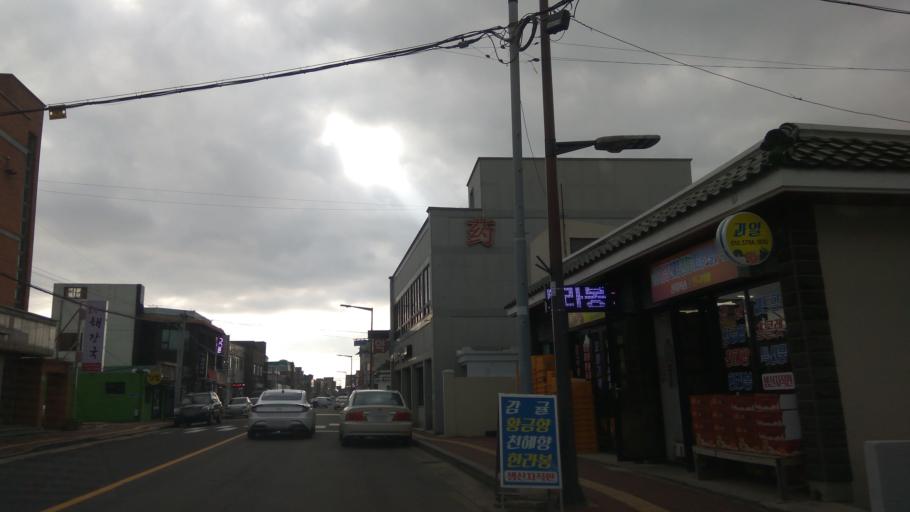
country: KR
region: Jeju-do
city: Jeju-si
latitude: 33.4635
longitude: 126.9336
